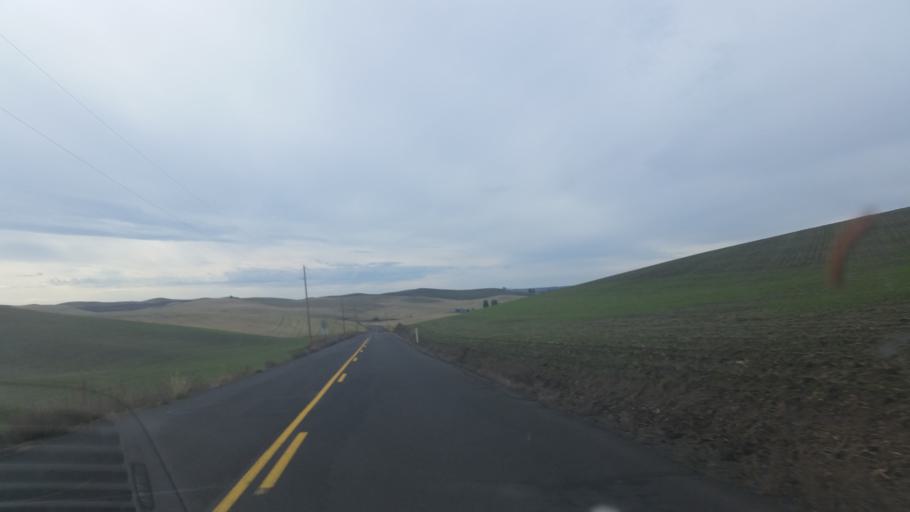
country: US
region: Washington
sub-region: Spokane County
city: Cheney
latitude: 47.3123
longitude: -117.4870
